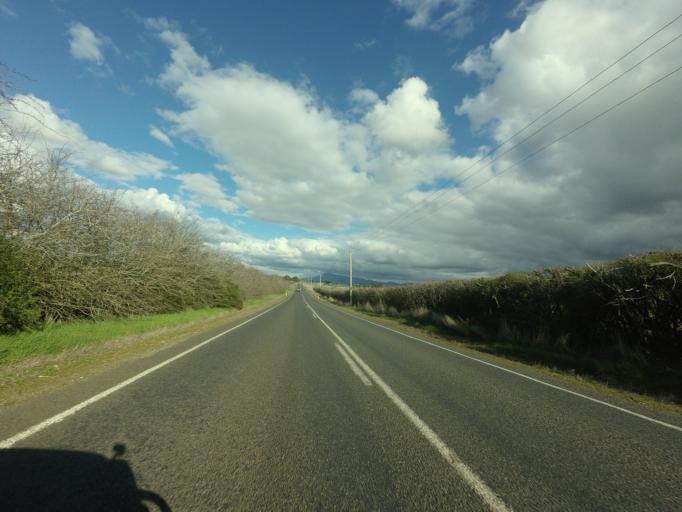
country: AU
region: Tasmania
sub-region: Northern Midlands
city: Longford
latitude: -41.7035
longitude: 147.0765
